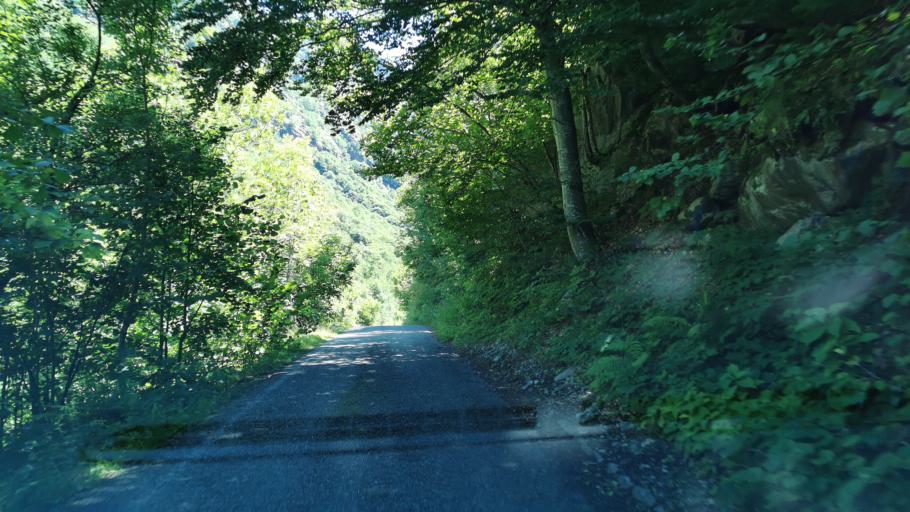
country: IT
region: Piedmont
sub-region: Provincia di Cuneo
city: Entracque
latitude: 44.1997
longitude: 7.3822
